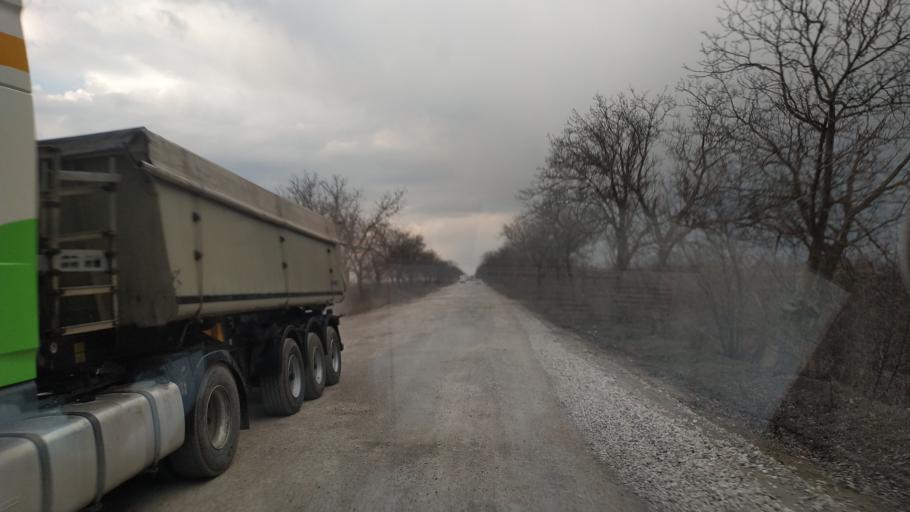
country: MD
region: Telenesti
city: Grigoriopol
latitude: 47.0485
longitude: 29.2935
